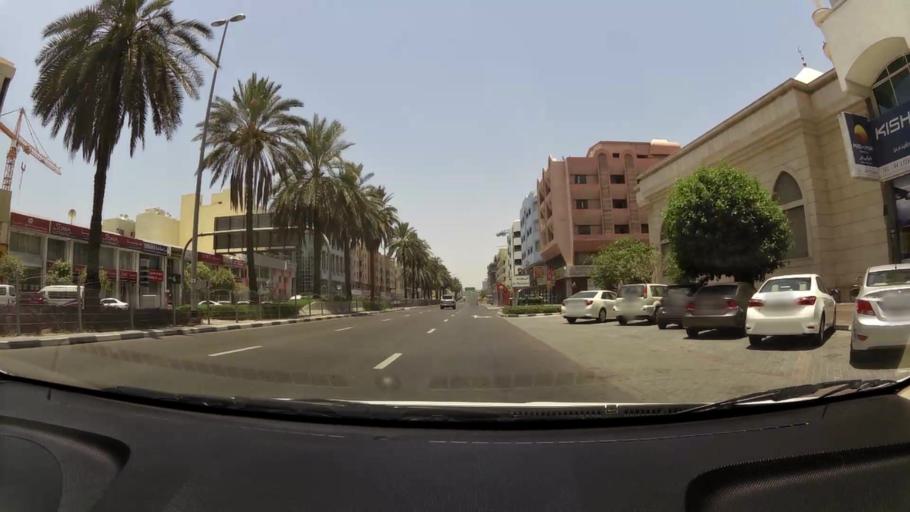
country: AE
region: Ash Shariqah
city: Sharjah
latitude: 25.2711
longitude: 55.3164
